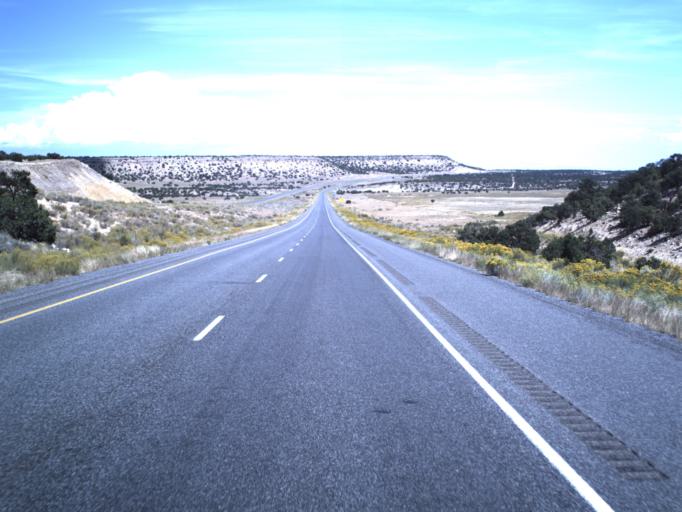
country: US
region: Utah
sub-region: Emery County
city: Castle Dale
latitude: 38.8989
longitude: -110.5733
